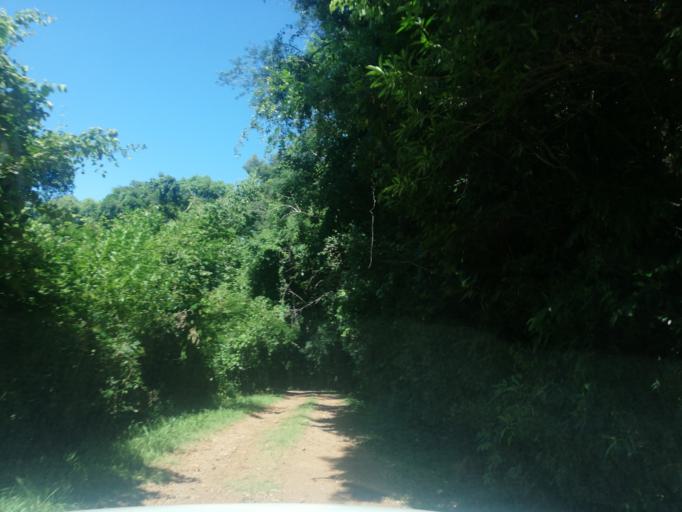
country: AR
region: Misiones
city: Cerro Azul
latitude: -27.7420
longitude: -55.5718
